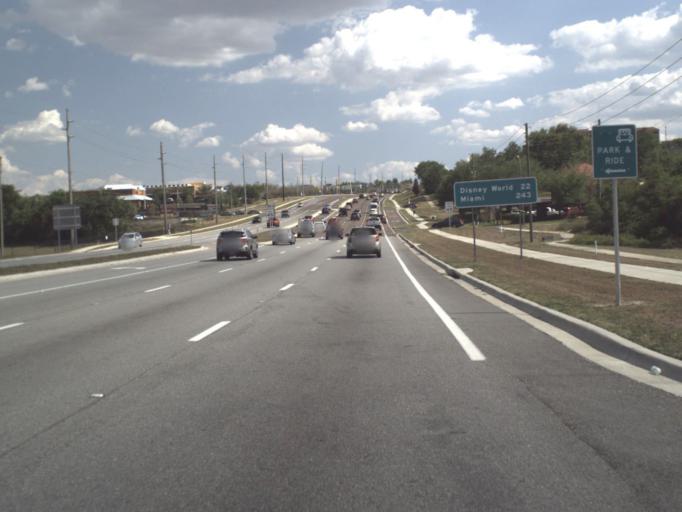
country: US
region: Florida
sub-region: Lake County
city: Clermont
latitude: 28.5407
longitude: -81.7404
